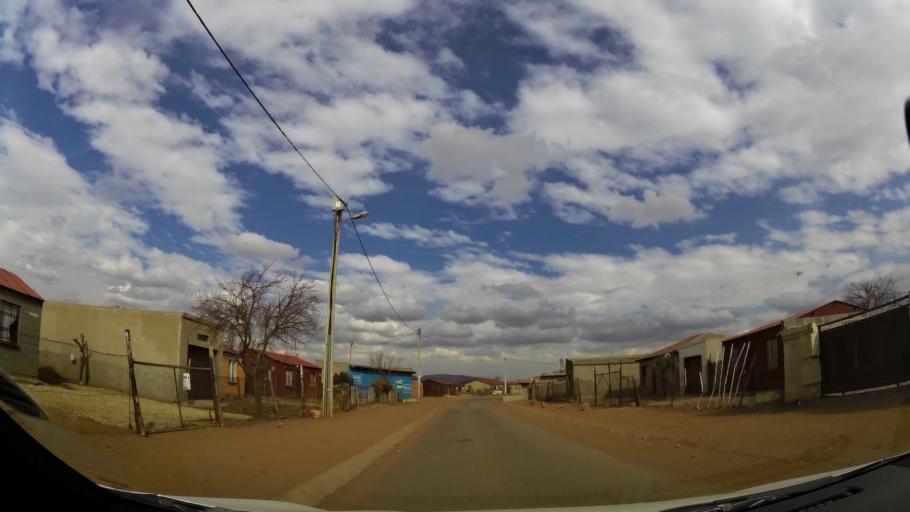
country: ZA
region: Gauteng
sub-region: Ekurhuleni Metropolitan Municipality
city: Germiston
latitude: -26.4105
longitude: 28.1611
